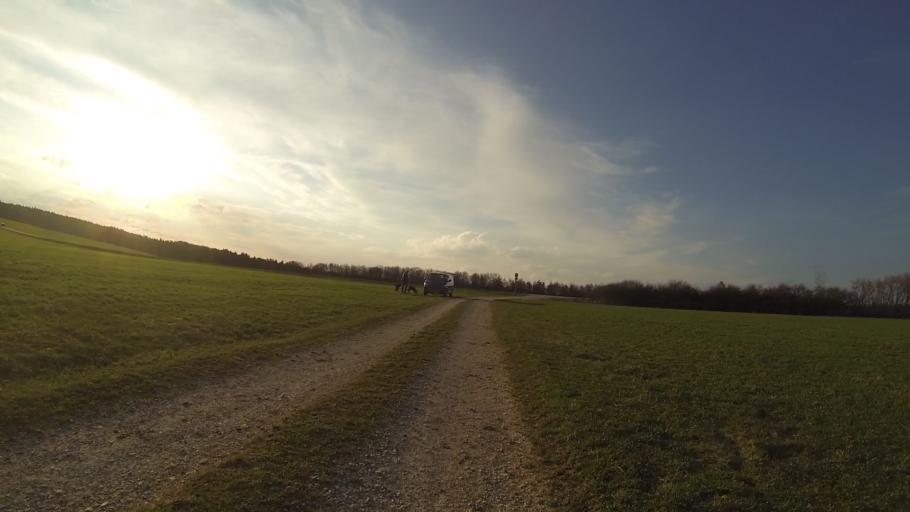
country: DE
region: Baden-Wuerttemberg
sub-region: Regierungsbezirk Stuttgart
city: Heidenheim an der Brenz
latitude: 48.7032
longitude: 10.1325
